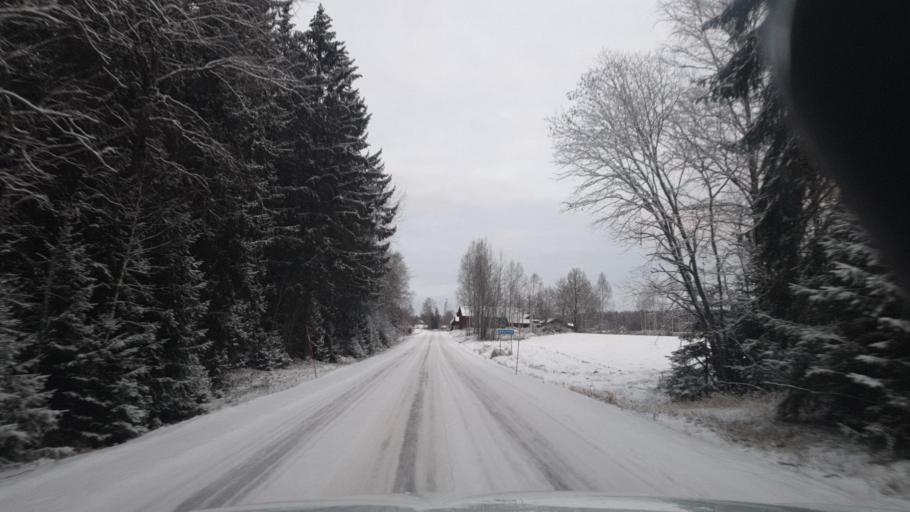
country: SE
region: Vaermland
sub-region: Eda Kommun
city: Charlottenberg
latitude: 59.7698
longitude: 12.2086
